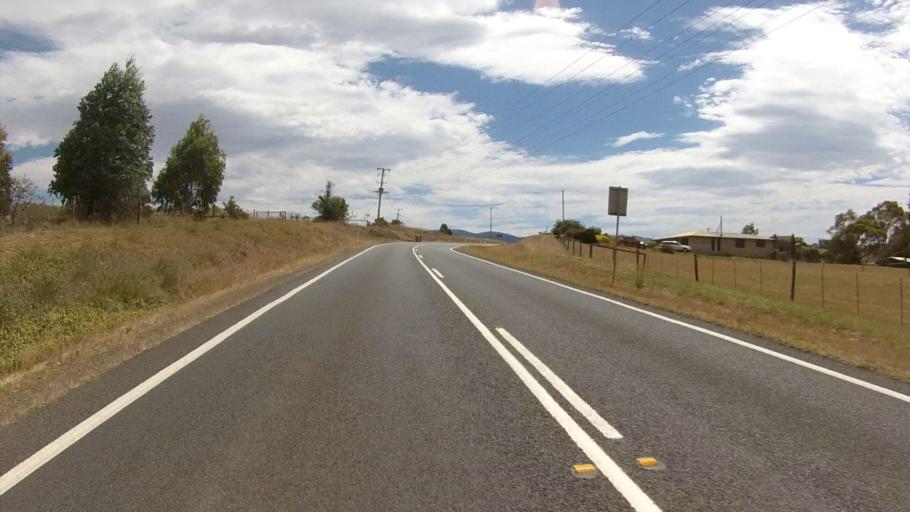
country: AU
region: Tasmania
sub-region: Brighton
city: Bridgewater
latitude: -42.6981
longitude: 147.2692
